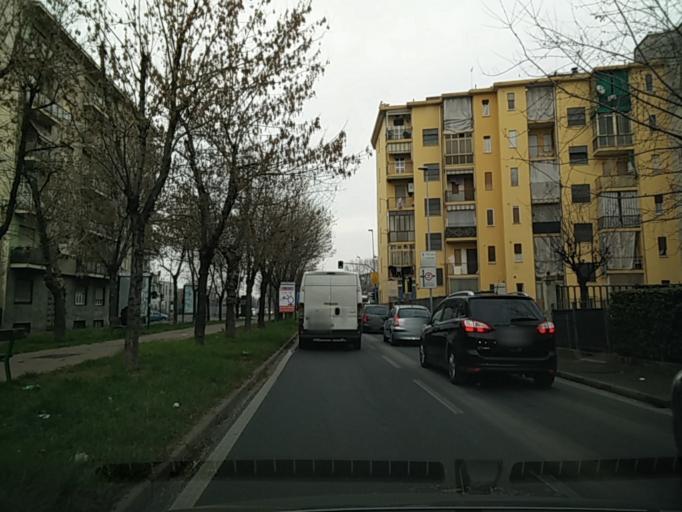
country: IT
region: Piedmont
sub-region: Provincia di Torino
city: Settimo Torinese
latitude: 45.1404
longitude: 7.7573
